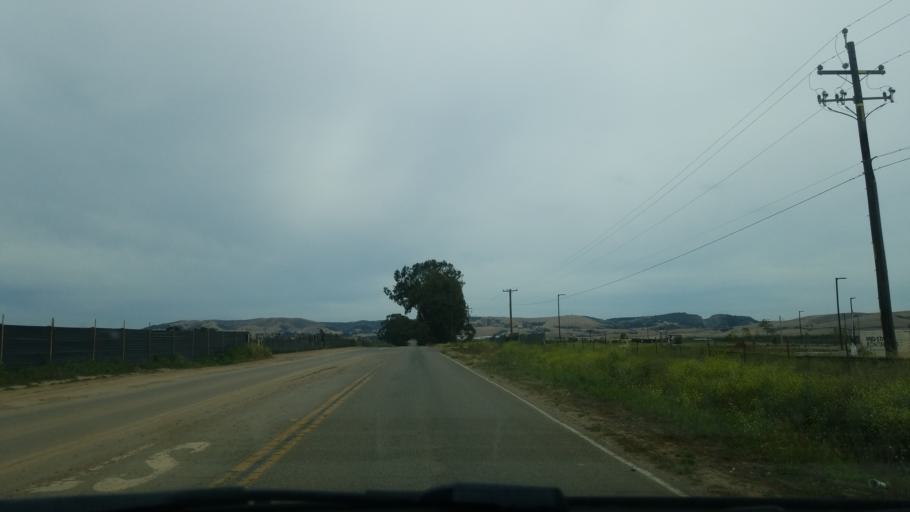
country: US
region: California
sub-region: Santa Barbara County
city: Santa Maria
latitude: 34.9192
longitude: -120.4902
